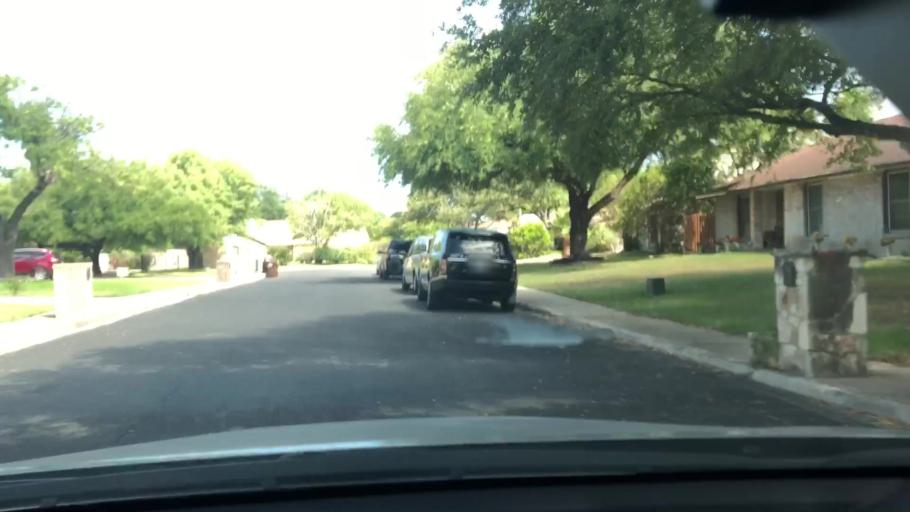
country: US
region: Texas
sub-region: Bexar County
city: Converse
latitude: 29.4875
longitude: -98.3391
